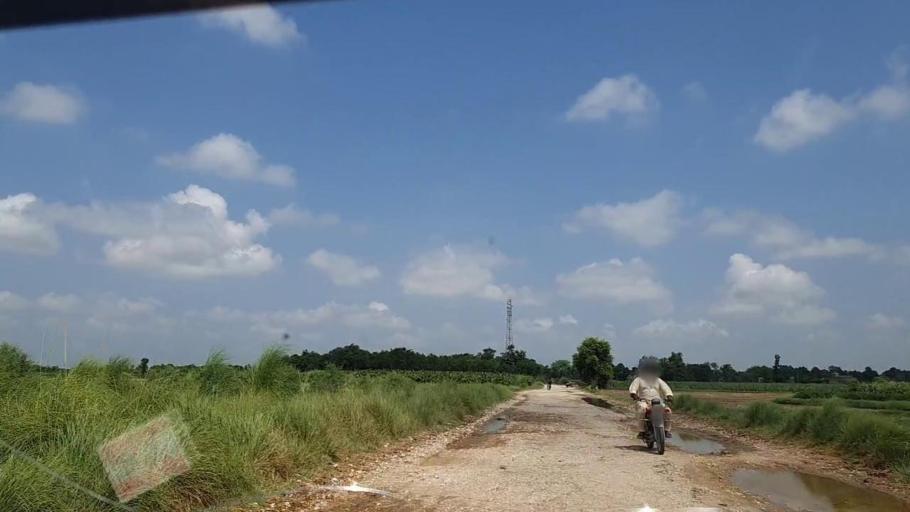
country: PK
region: Sindh
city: Tharu Shah
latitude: 26.9078
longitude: 68.0371
